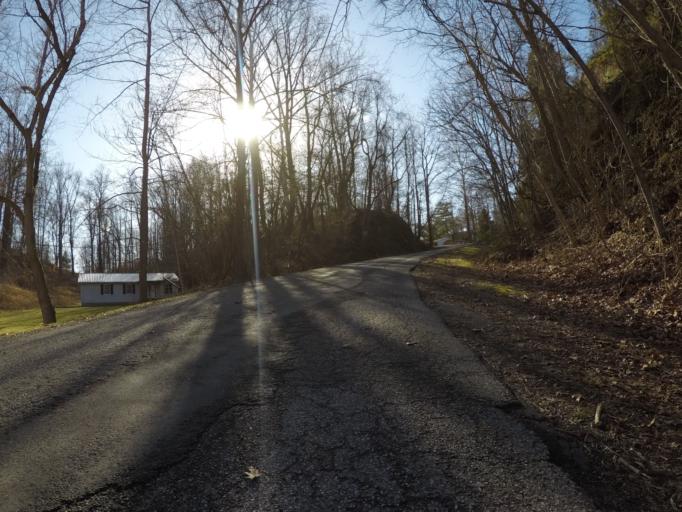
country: US
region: West Virginia
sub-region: Wayne County
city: Ceredo
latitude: 38.3892
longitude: -82.5615
